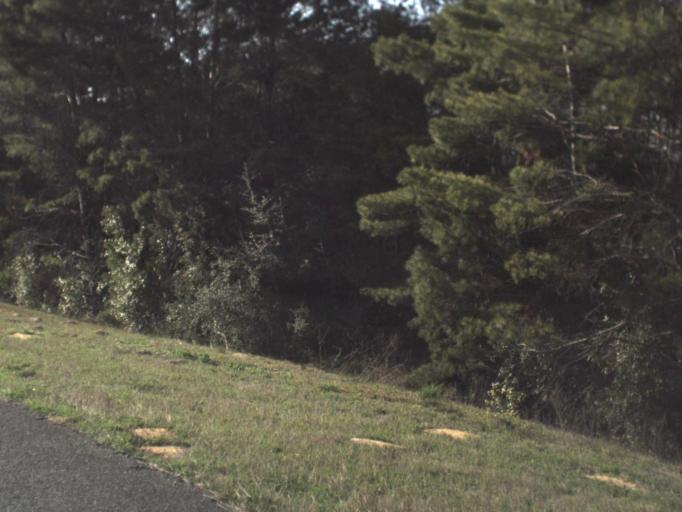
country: US
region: Florida
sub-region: Bay County
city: Lynn Haven
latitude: 30.4260
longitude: -85.6288
